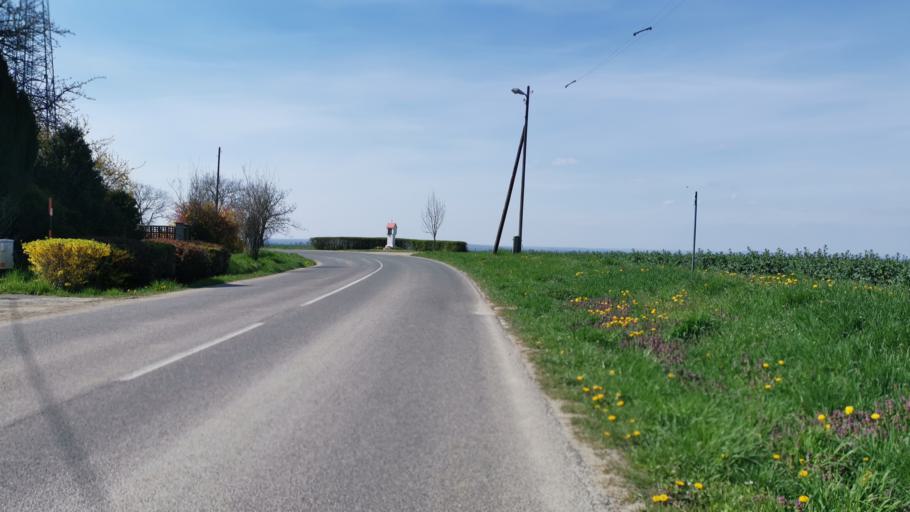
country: SK
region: Trnavsky
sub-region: Okres Skalica
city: Holic
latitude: 48.7548
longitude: 17.1919
